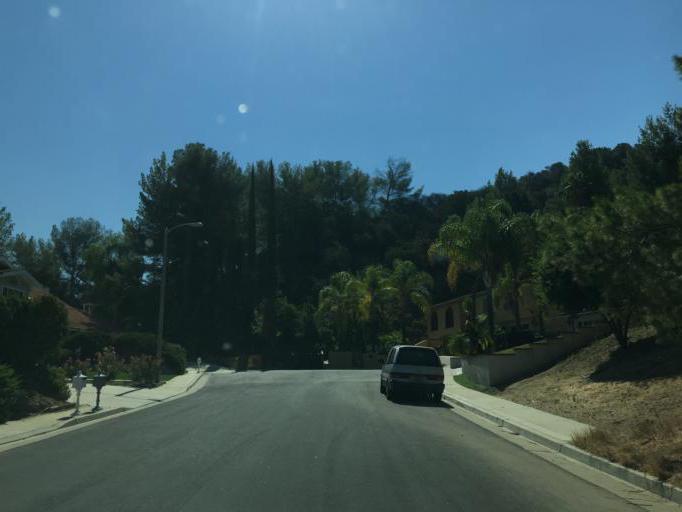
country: US
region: California
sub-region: Los Angeles County
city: Woodland Hills
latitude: 34.1410
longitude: -118.6003
